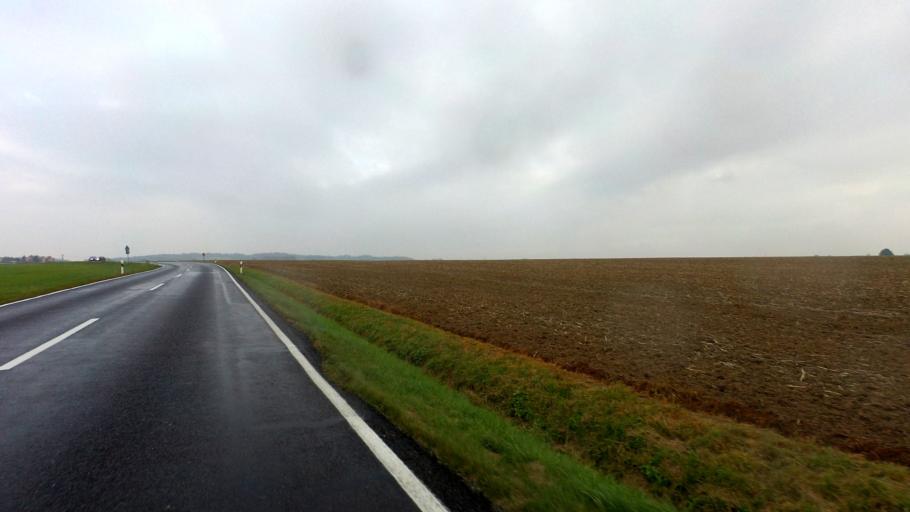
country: DE
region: Saxony
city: Arnsdorf
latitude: 51.1086
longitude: 13.9721
